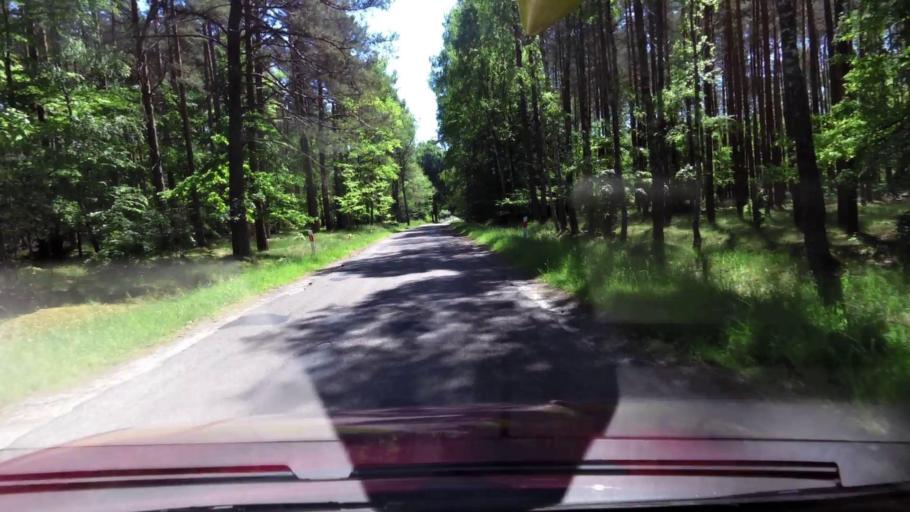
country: PL
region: West Pomeranian Voivodeship
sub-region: Powiat koszalinski
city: Bobolice
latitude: 54.0528
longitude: 16.5815
